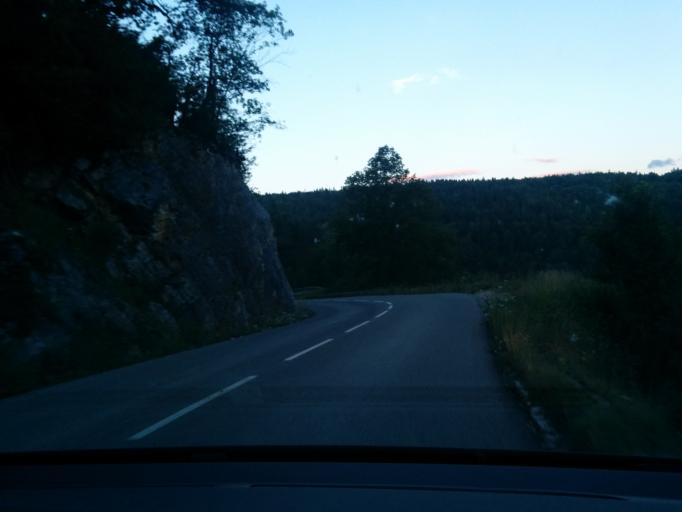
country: FR
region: Franche-Comte
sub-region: Departement du Jura
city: Valfin-les-Saint-Claude
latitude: 46.4403
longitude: 5.8111
